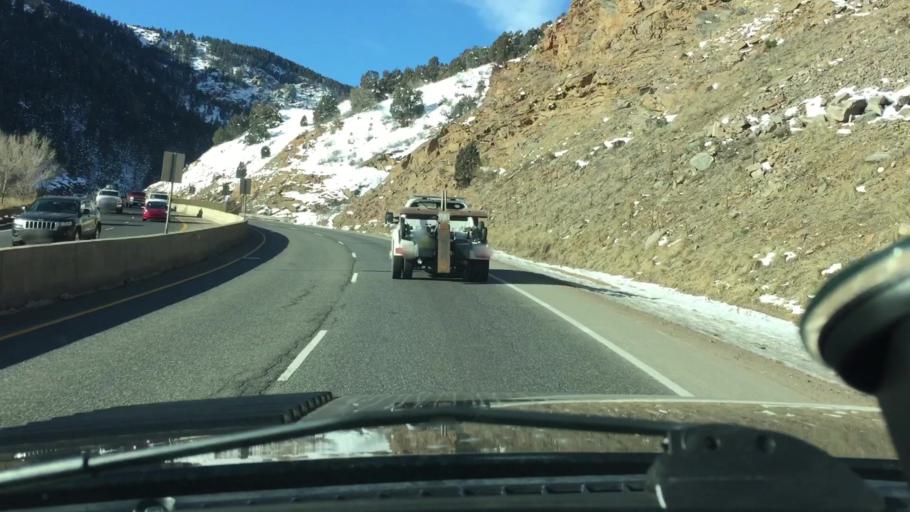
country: US
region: Colorado
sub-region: Jefferson County
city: Indian Hills
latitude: 39.6212
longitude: -105.2008
